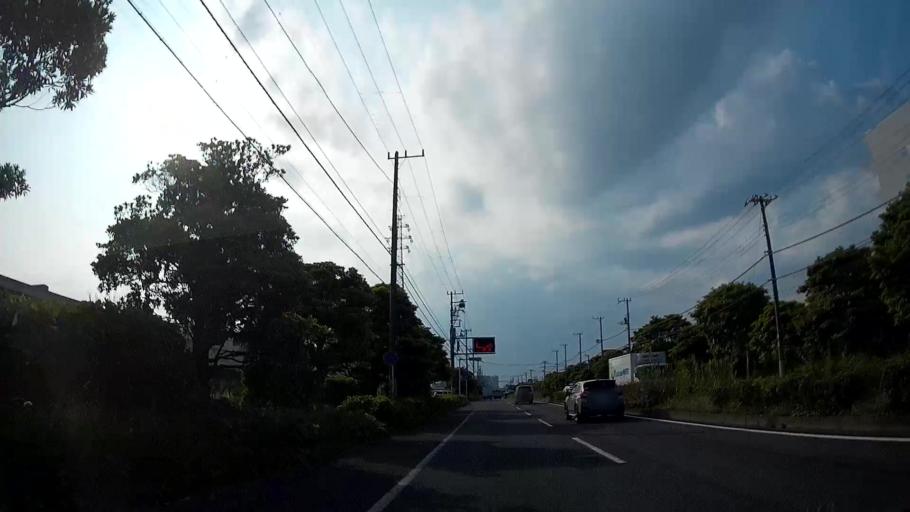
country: JP
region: Chiba
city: Funabashi
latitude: 35.6660
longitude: 140.0073
